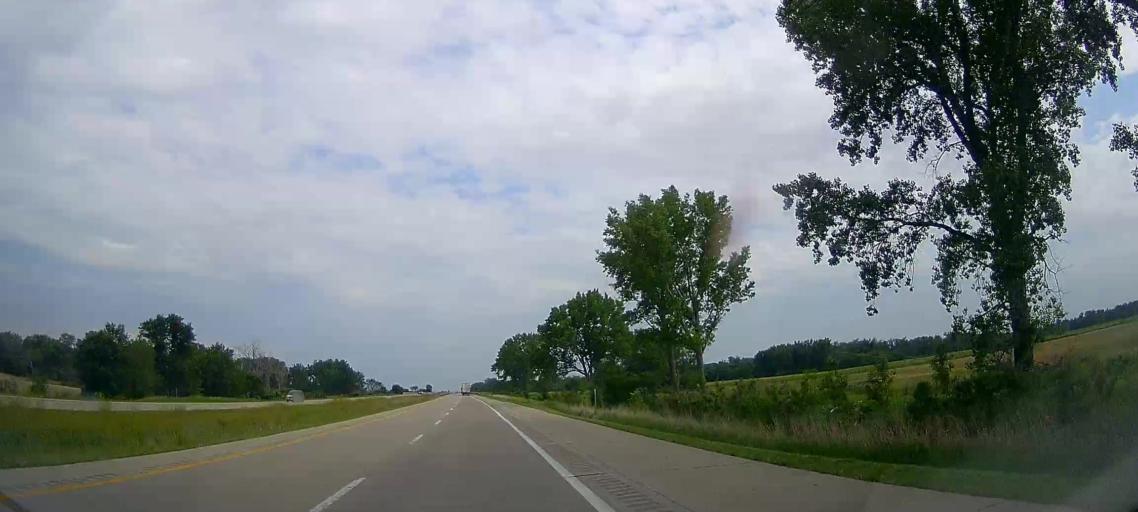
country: US
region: Nebraska
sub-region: Burt County
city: Tekamah
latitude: 41.8233
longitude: -96.0751
